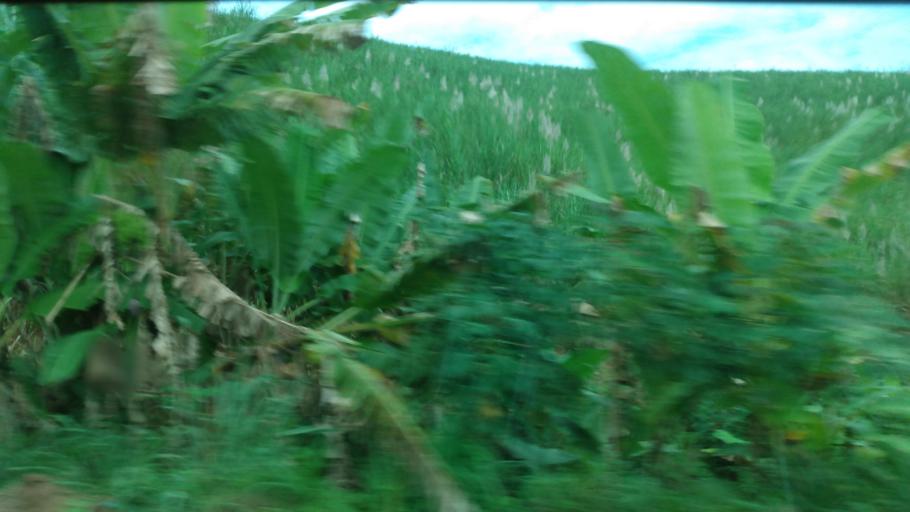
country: BR
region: Pernambuco
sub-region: Maraial
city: Maraial
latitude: -8.7165
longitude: -35.7801
